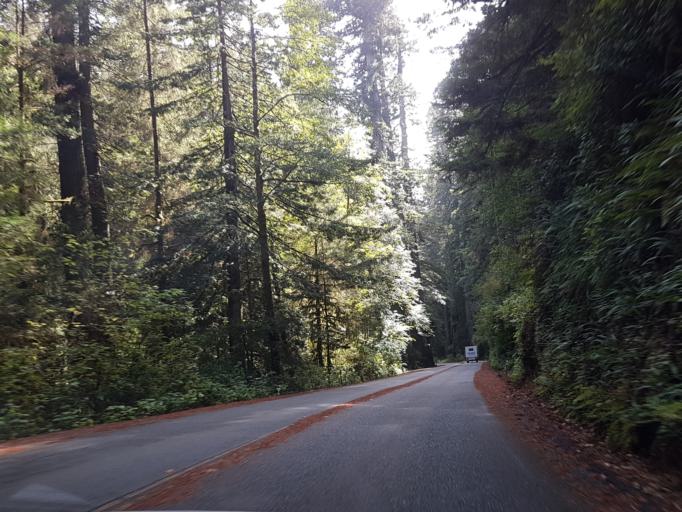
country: US
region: California
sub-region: Del Norte County
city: Bertsch-Oceanview
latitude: 41.4422
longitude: -124.0410
